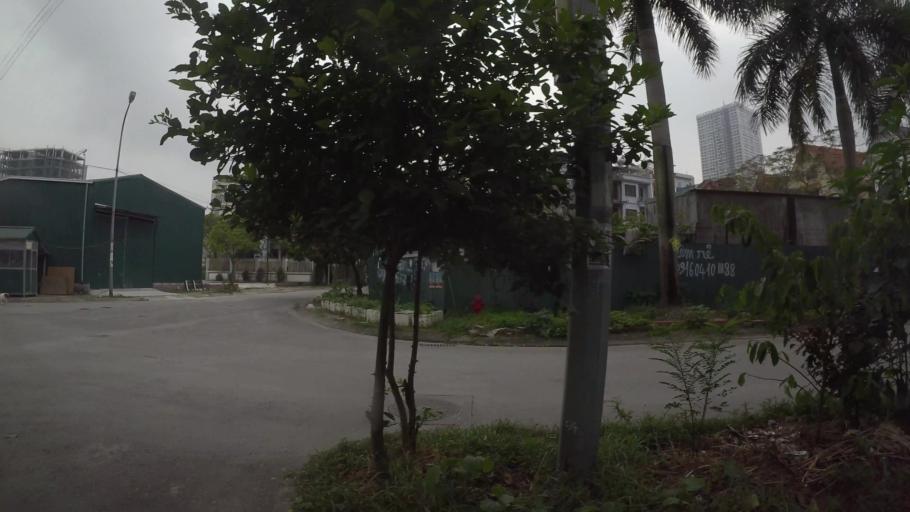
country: VN
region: Ha Noi
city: Ha Dong
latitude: 20.9829
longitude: 105.7667
